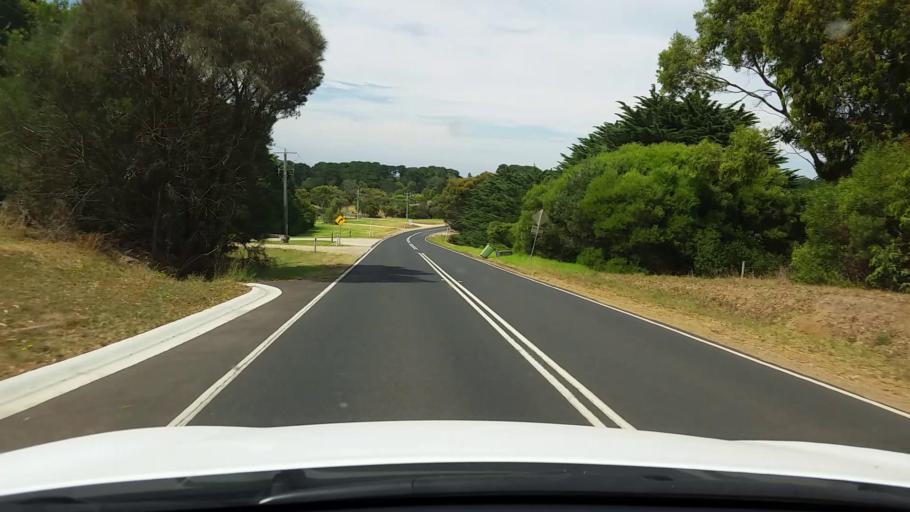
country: AU
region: Victoria
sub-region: Mornington Peninsula
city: Merricks
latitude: -38.4600
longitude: 145.0207
